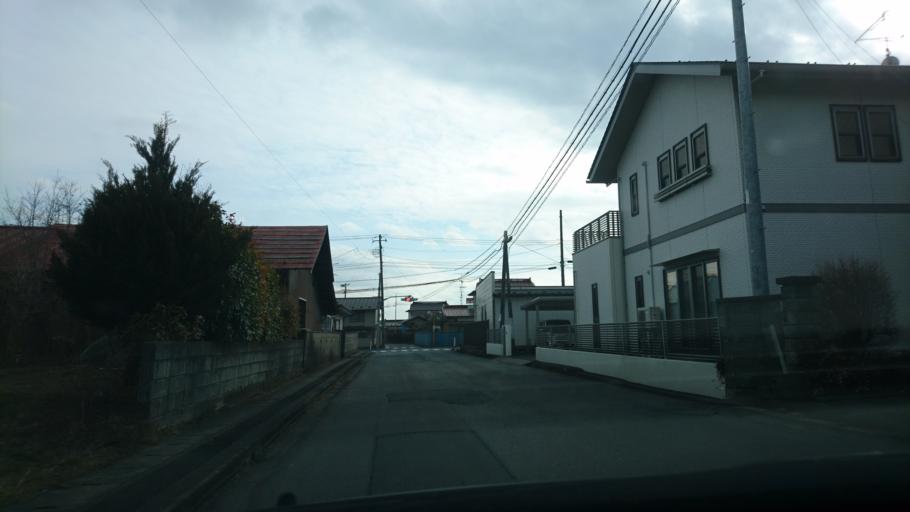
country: JP
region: Iwate
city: Ichinoseki
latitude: 38.8485
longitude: 141.1721
